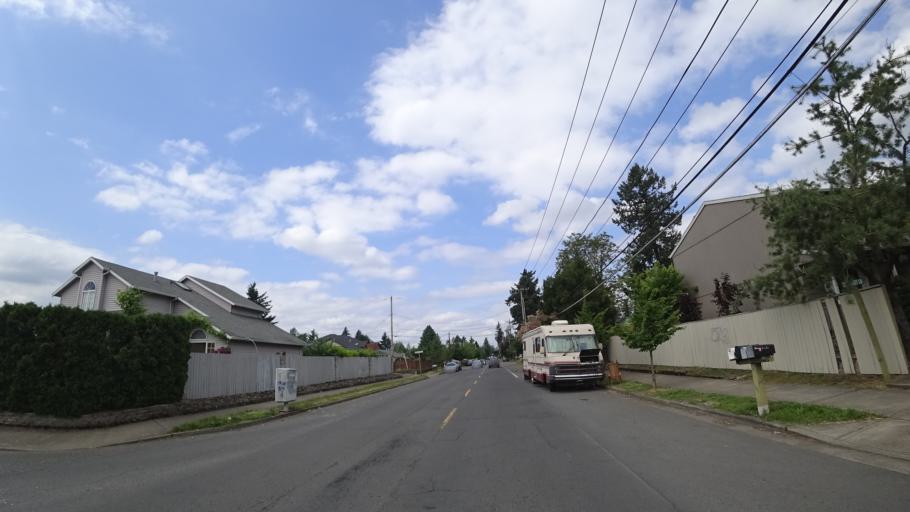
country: US
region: Oregon
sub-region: Multnomah County
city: Gresham
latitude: 45.5069
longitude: -122.4847
